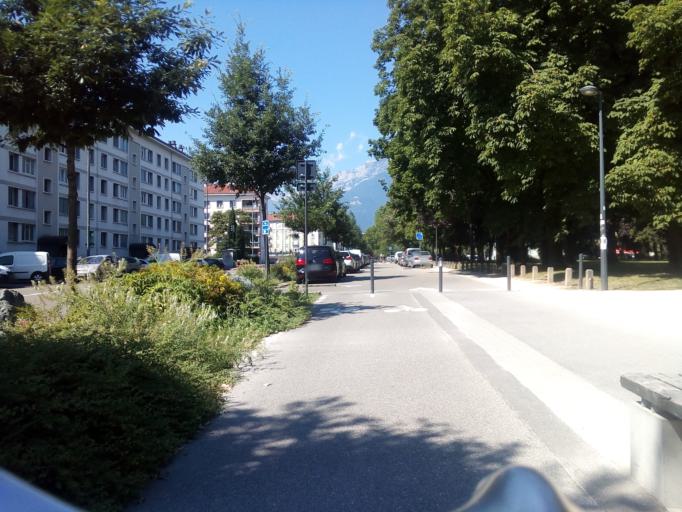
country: FR
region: Rhone-Alpes
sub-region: Departement de l'Isere
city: La Tronche
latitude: 45.1844
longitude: 5.7404
